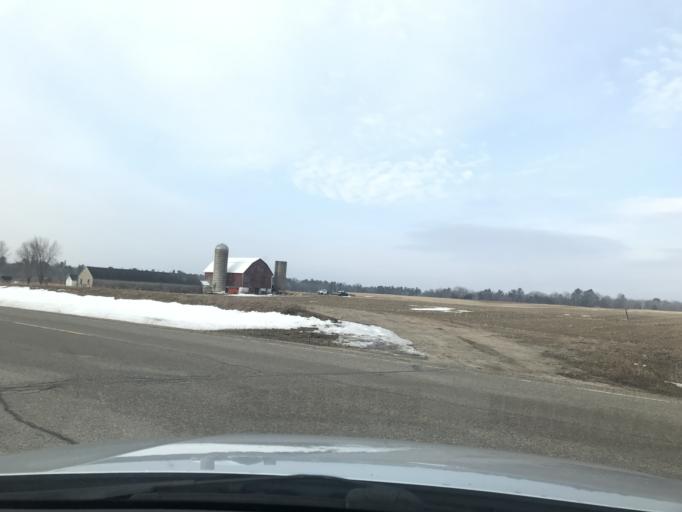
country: US
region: Wisconsin
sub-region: Oconto County
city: Oconto Falls
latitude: 44.8299
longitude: -88.1885
